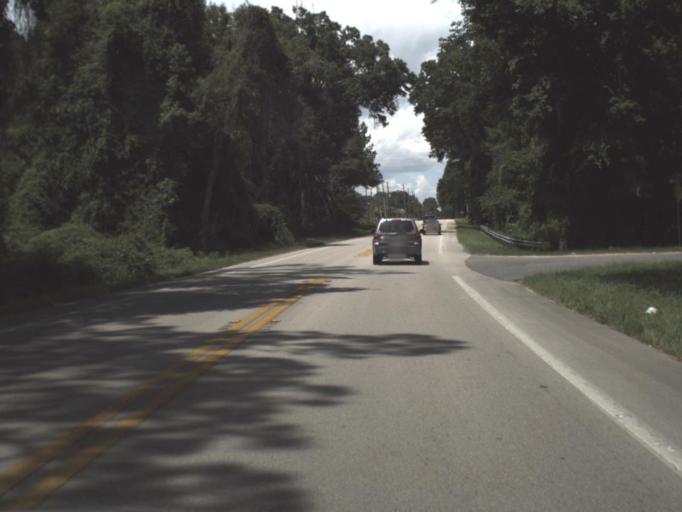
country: US
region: Florida
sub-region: Alachua County
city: High Springs
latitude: 29.8122
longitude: -82.6057
